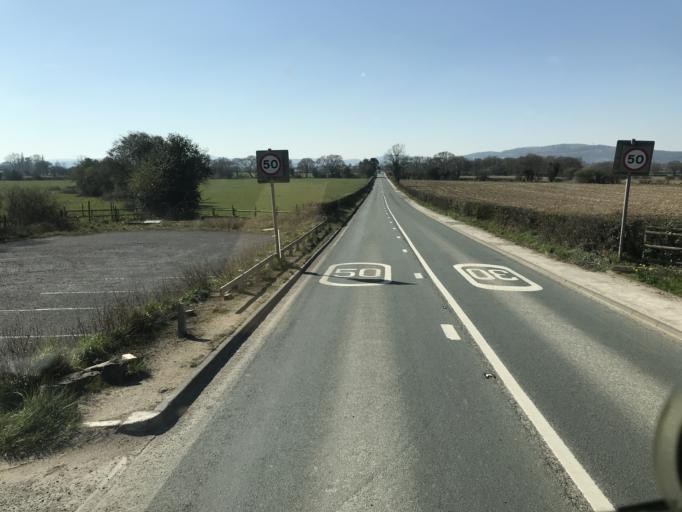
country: GB
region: Wales
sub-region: Wrexham
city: Gresford
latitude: 53.1030
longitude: -2.9807
